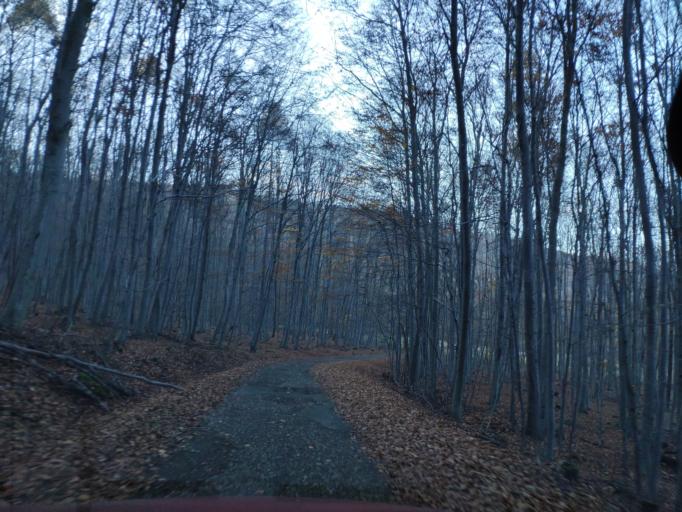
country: SK
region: Kosicky
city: Secovce
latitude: 48.5851
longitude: 21.5060
